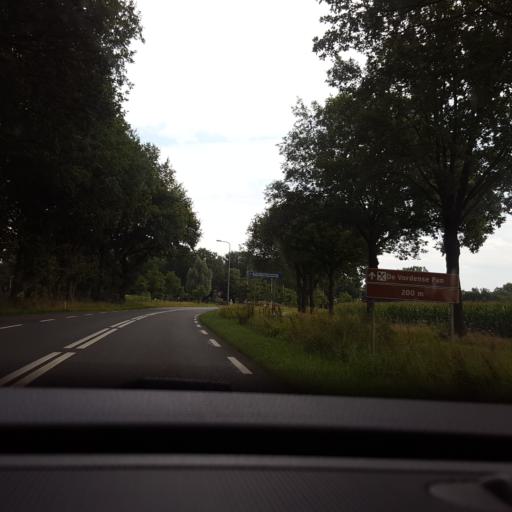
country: NL
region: Gelderland
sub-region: Gemeente Bronckhorst
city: Hengelo
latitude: 52.0970
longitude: 6.3078
